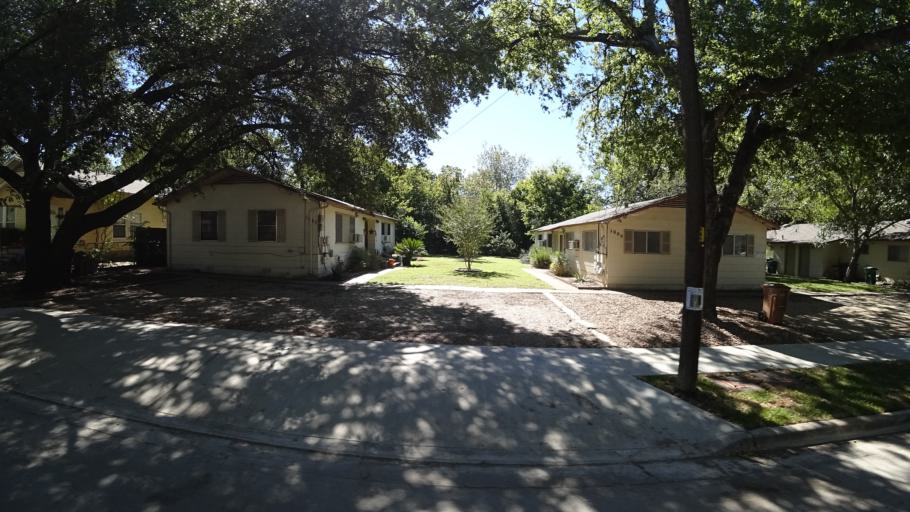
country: US
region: Texas
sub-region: Travis County
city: Austin
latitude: 30.3313
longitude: -97.7263
